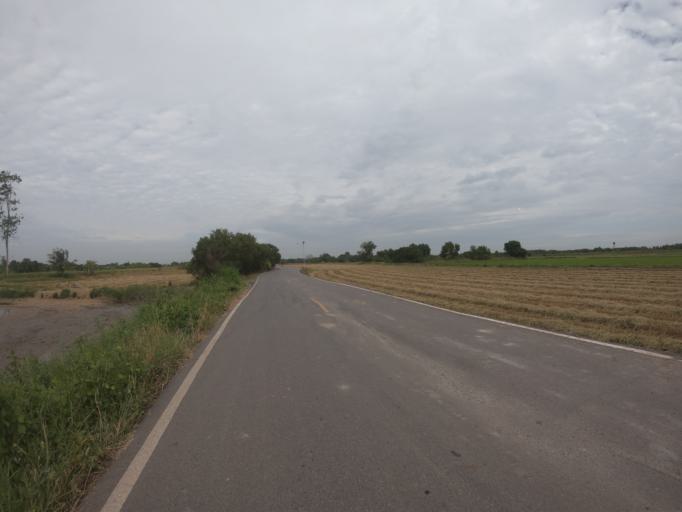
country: TH
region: Pathum Thani
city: Nong Suea
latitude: 14.0338
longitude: 100.8782
